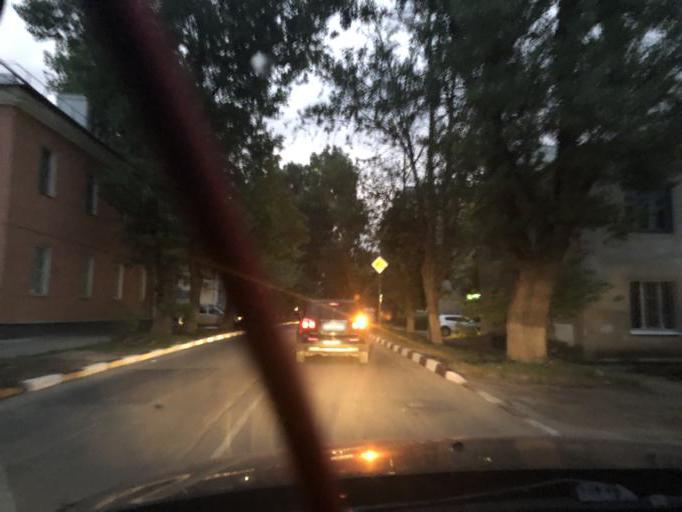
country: RU
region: Tula
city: Gorelki
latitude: 54.2267
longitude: 37.6174
